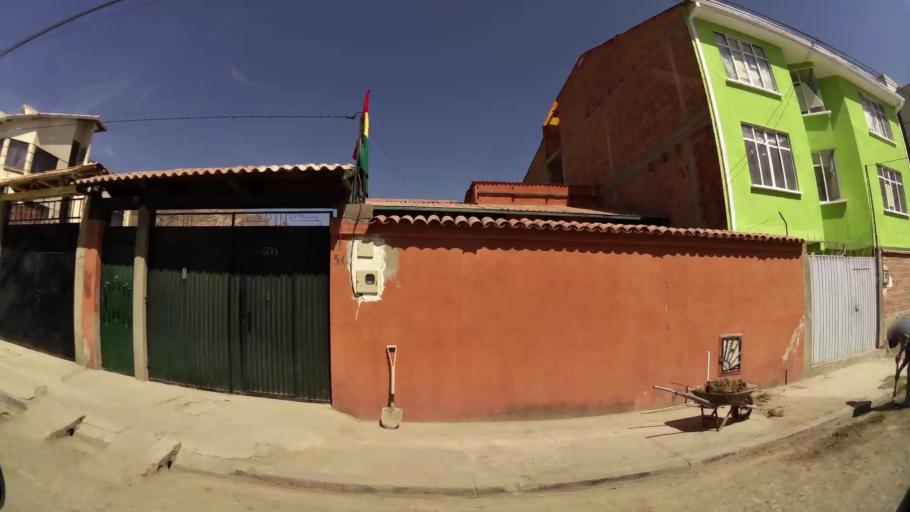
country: BO
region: La Paz
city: La Paz
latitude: -16.5403
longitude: -68.0496
